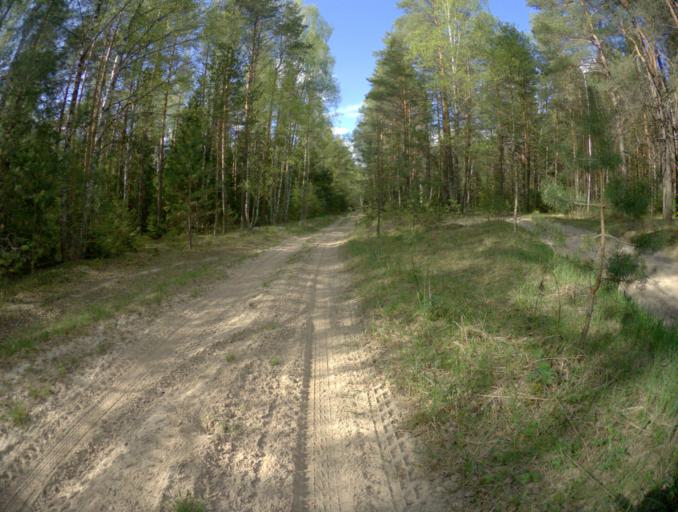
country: RU
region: Vladimir
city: Golovino
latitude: 55.9083
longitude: 40.4426
